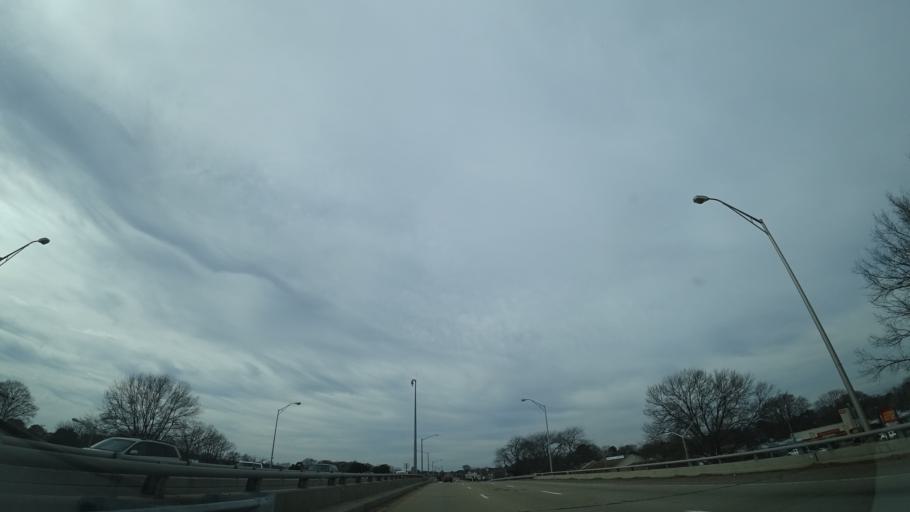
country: US
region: Virginia
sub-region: City of Hampton
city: Hampton
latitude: 37.0435
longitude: -76.3477
